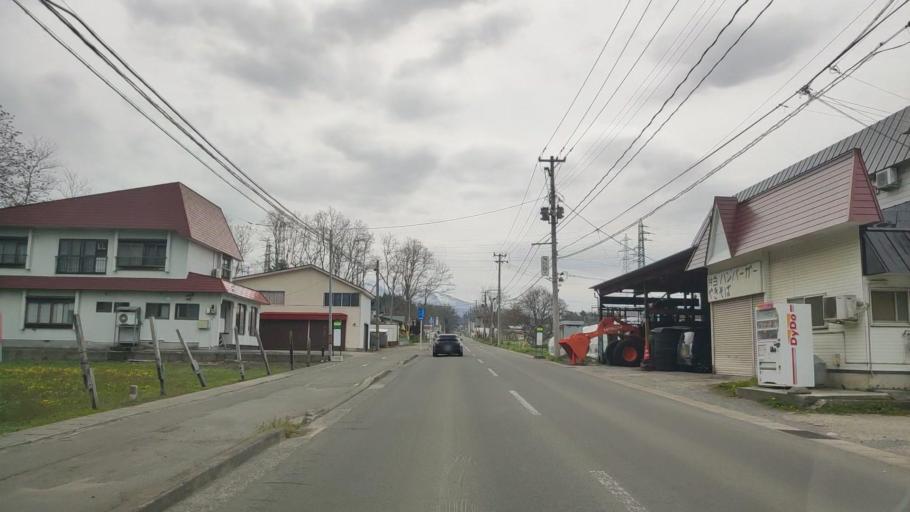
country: JP
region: Aomori
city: Aomori Shi
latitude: 40.7803
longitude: 140.7927
